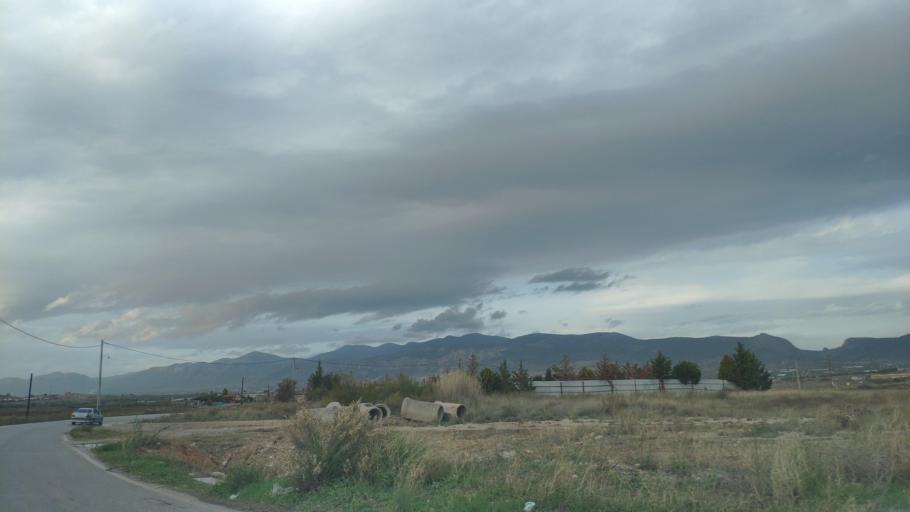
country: GR
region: Attica
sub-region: Nomarchia Dytikis Attikis
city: Megara
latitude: 37.9805
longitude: 23.3840
